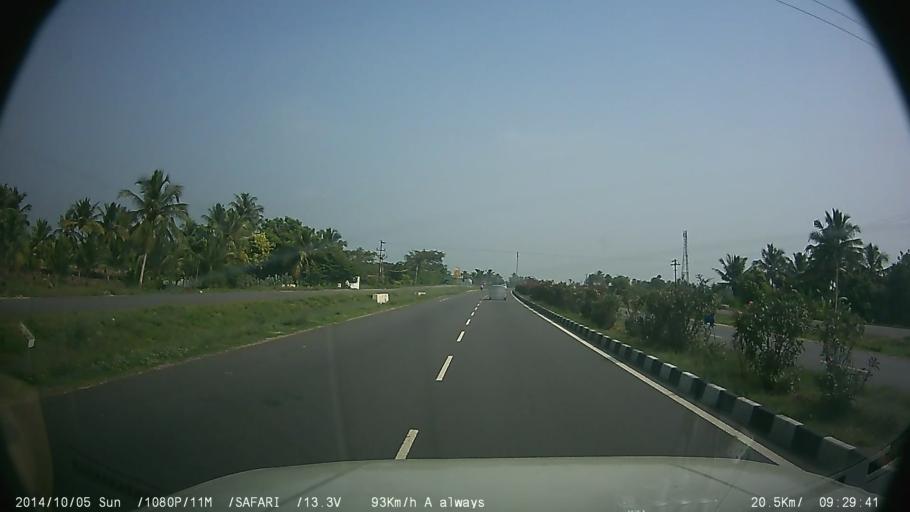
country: IN
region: Tamil Nadu
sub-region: Erode
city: Erode
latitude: 11.3629
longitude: 77.6467
